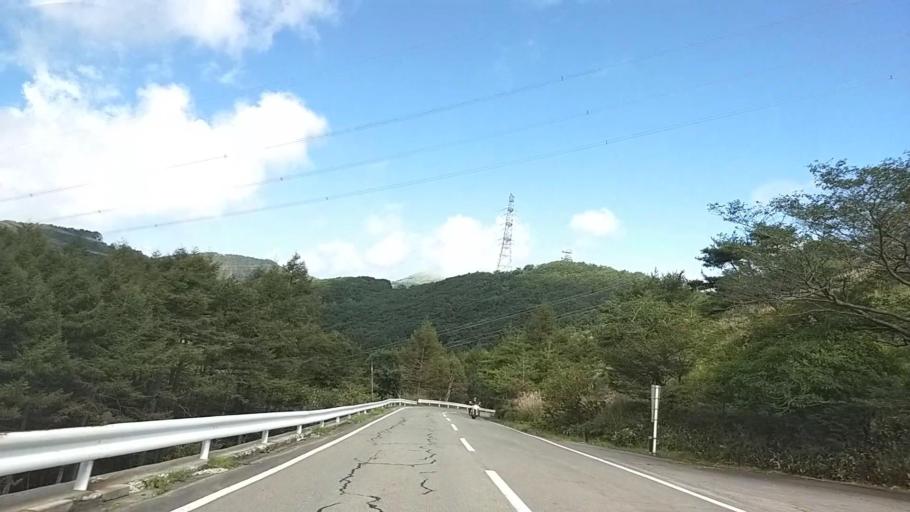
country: JP
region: Nagano
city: Suwa
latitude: 36.1391
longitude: 138.1500
